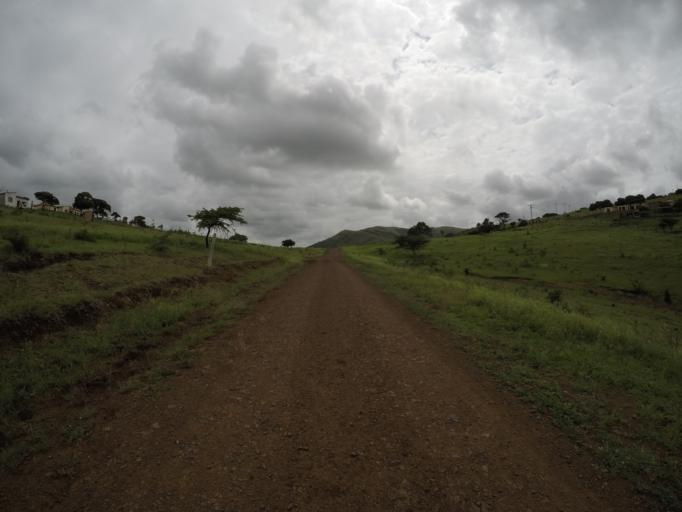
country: ZA
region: KwaZulu-Natal
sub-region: uThungulu District Municipality
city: Empangeni
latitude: -28.6184
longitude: 31.8920
